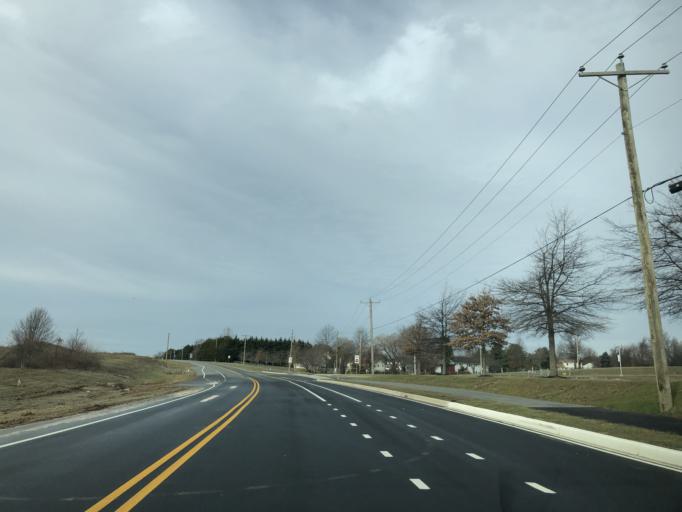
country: US
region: Delaware
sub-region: New Castle County
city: Middletown
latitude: 39.5258
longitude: -75.6670
